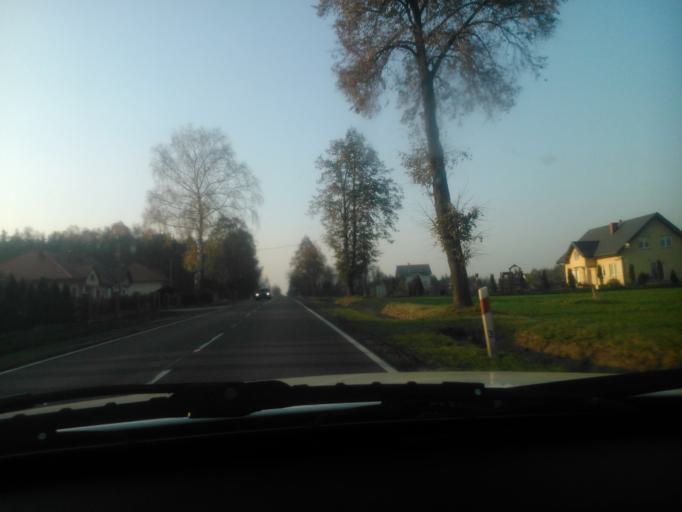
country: PL
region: Masovian Voivodeship
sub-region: Powiat mlawski
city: Szydlowo
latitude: 53.0857
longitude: 20.4391
